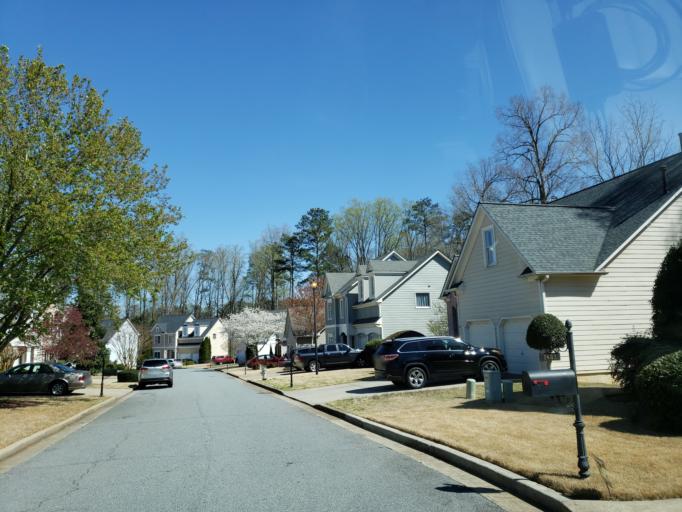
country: US
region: Georgia
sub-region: Cobb County
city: Marietta
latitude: 33.9875
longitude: -84.5057
